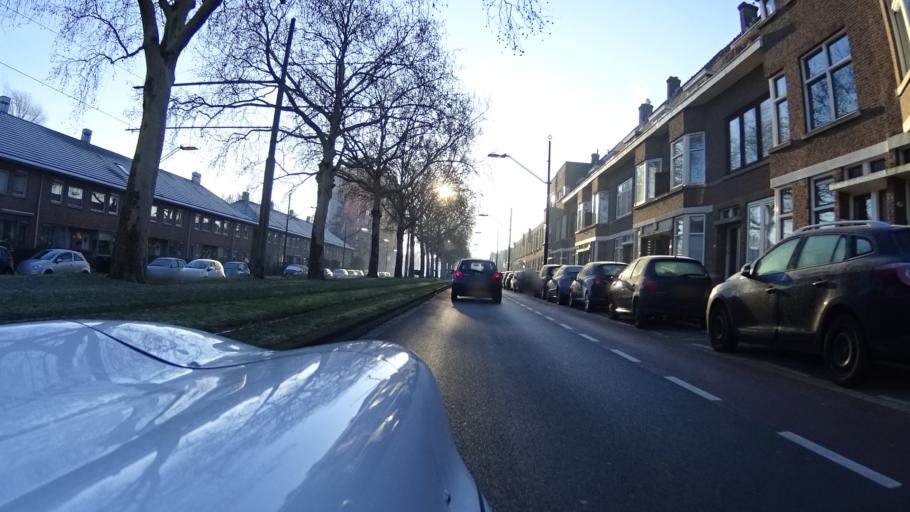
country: NL
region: South Holland
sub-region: Gemeente Barendrecht
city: Barendrecht
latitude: 51.8815
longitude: 4.5052
